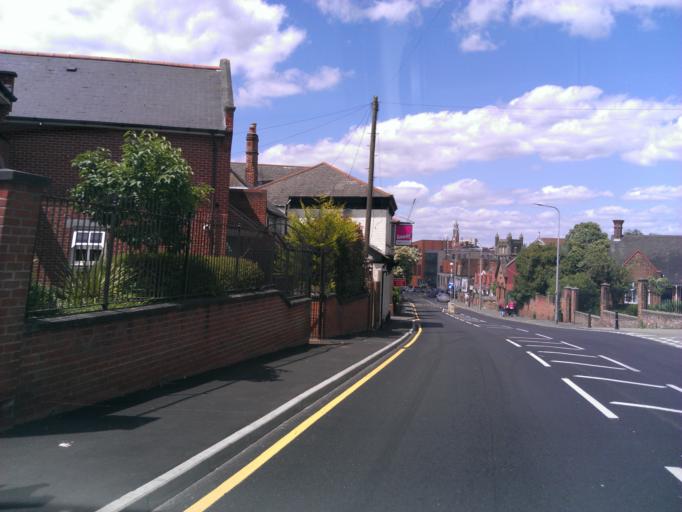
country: GB
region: England
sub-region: Essex
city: Colchester
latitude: 51.8848
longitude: 0.9072
